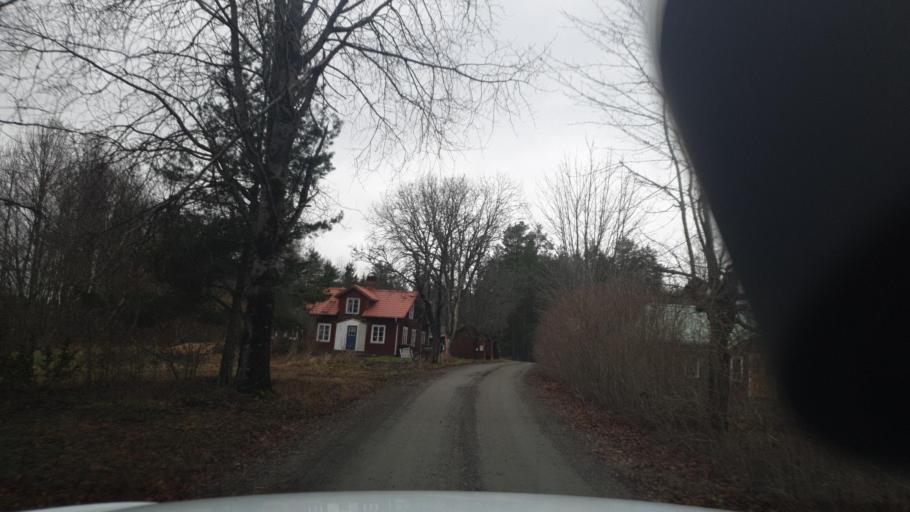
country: SE
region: Vaermland
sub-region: Karlstads Kommun
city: Edsvalla
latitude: 59.6206
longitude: 13.0644
